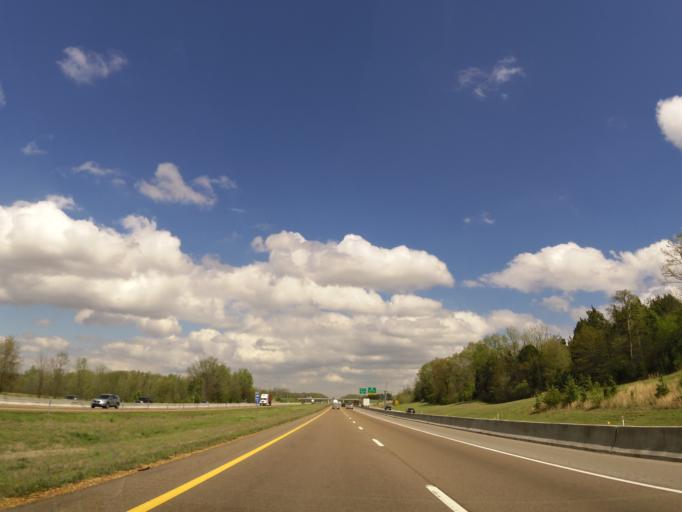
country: US
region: Tennessee
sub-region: Shelby County
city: Arlington
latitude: 35.2586
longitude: -89.6717
